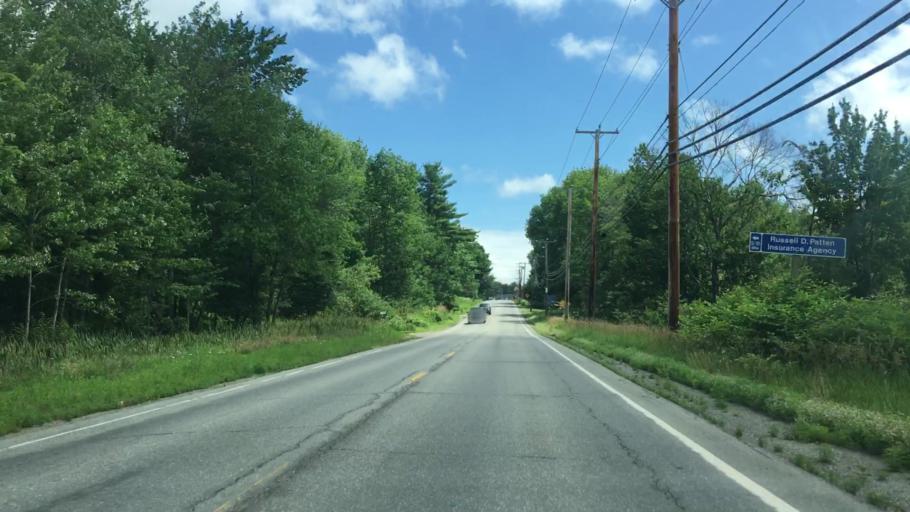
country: US
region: Maine
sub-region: Penobscot County
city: Hermon
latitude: 44.8092
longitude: -68.9179
